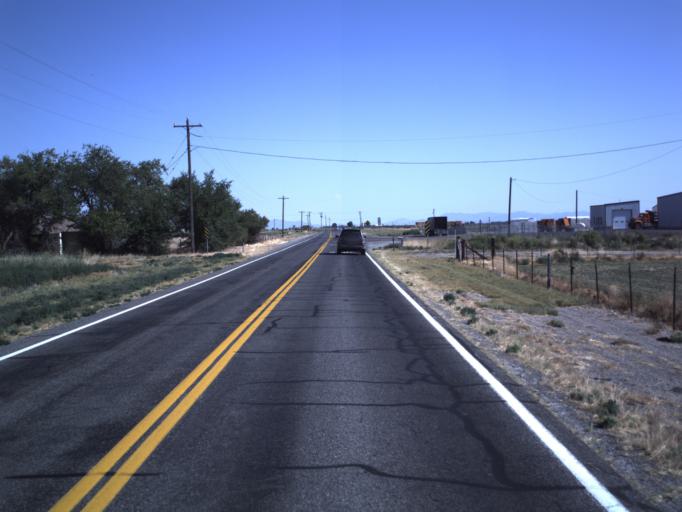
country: US
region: Utah
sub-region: Millard County
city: Delta
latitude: 39.3265
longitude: -112.6523
